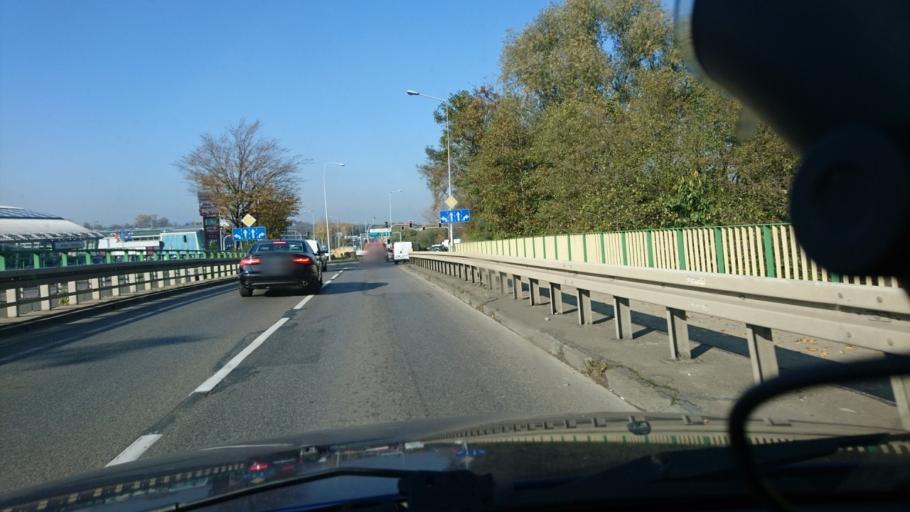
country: PL
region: Silesian Voivodeship
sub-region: Bielsko-Biala
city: Bielsko-Biala
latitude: 49.8384
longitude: 19.0389
